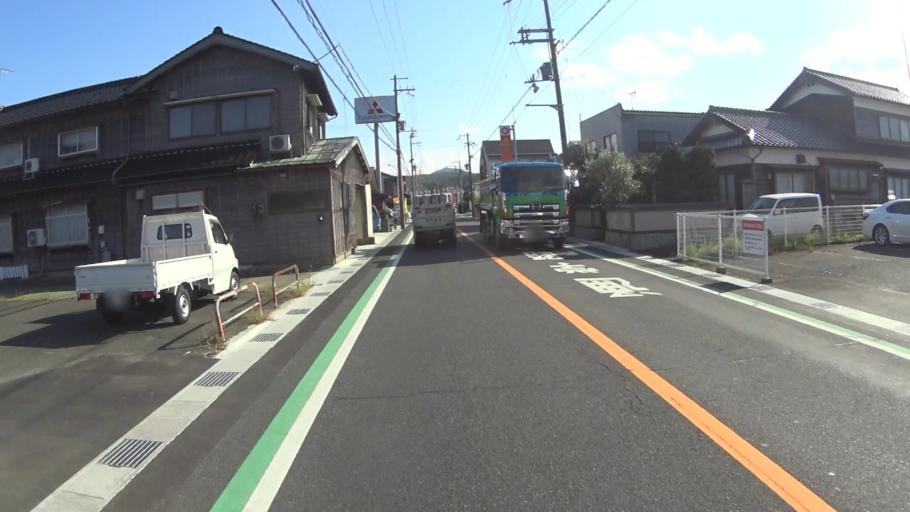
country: JP
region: Kyoto
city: Miyazu
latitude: 35.6742
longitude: 135.0281
